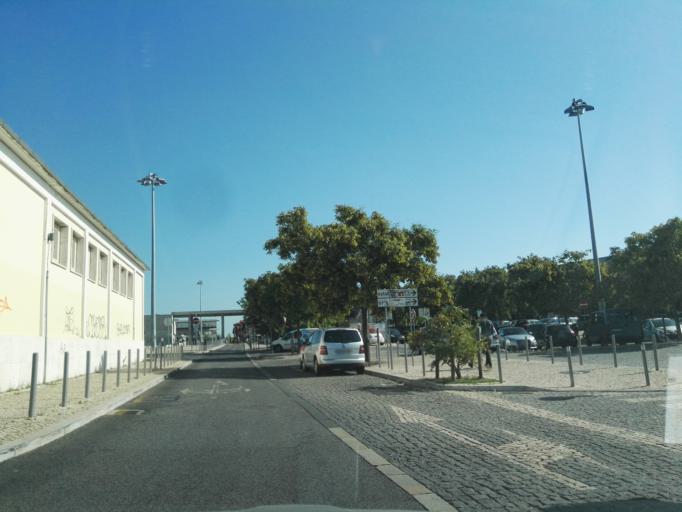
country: PT
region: Lisbon
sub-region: Lisbon
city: Lisbon
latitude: 38.7055
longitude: -9.1465
